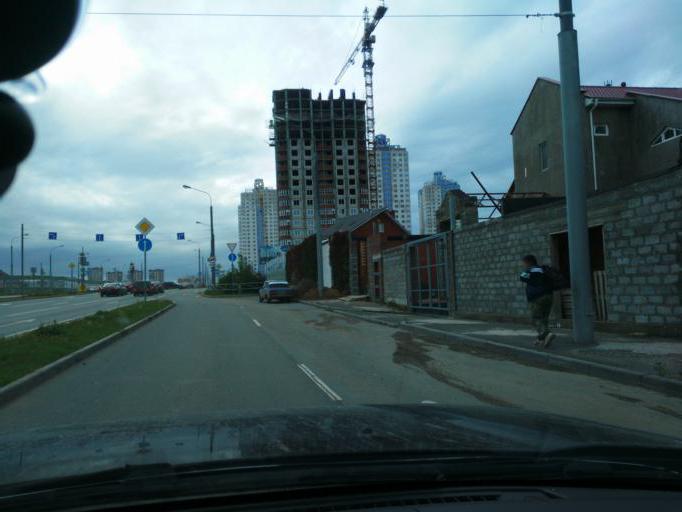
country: RU
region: Perm
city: Perm
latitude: 58.0052
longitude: 56.3295
